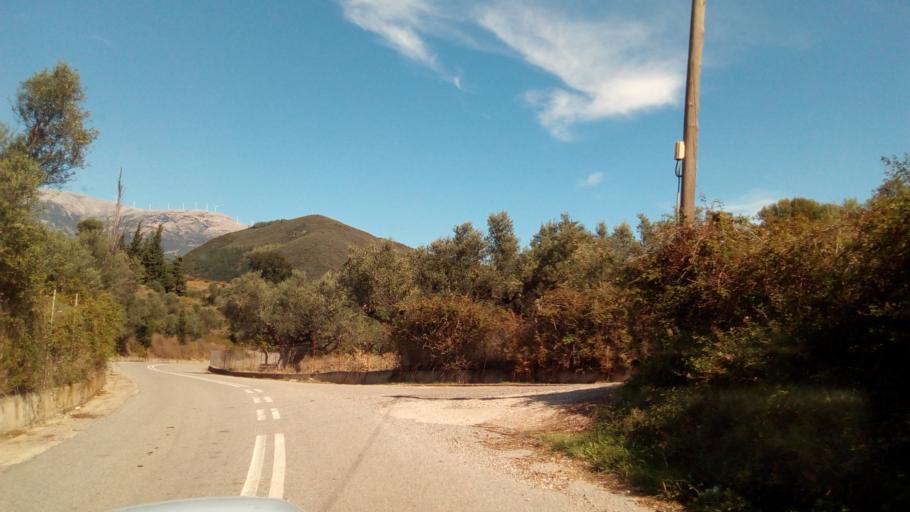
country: GR
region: West Greece
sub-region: Nomos Aitolias kai Akarnanias
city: Antirrio
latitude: 38.3663
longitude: 21.7679
